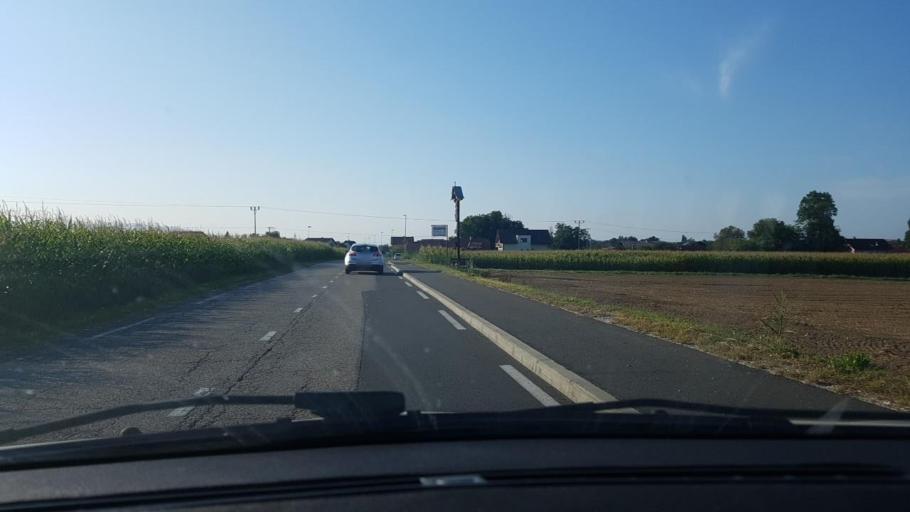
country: SI
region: Ptuj
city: Ptuj
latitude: 46.3879
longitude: 15.8721
